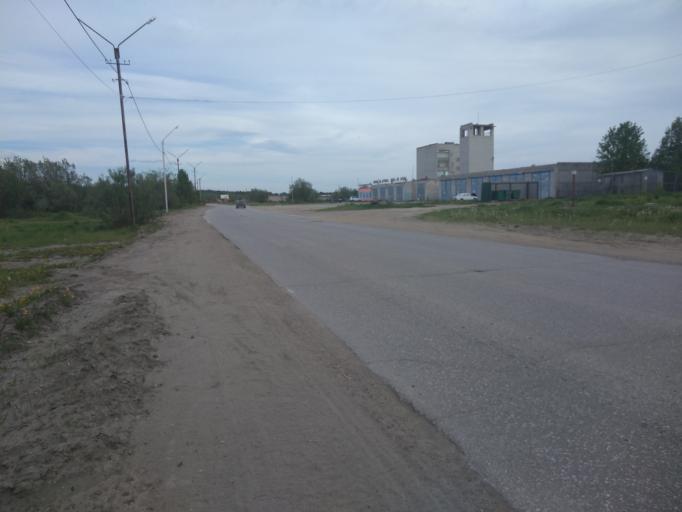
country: RU
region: Komi Republic
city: Pechora
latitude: 65.1441
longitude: 57.2430
